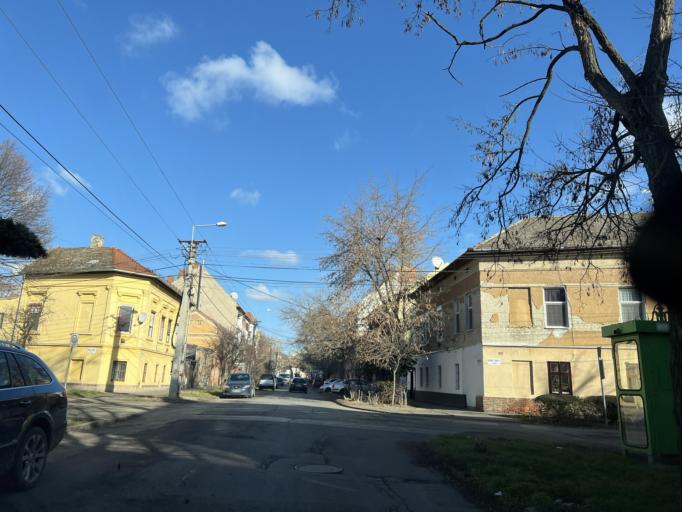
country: HU
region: Csongrad
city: Szeged
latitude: 46.2511
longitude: 20.1340
